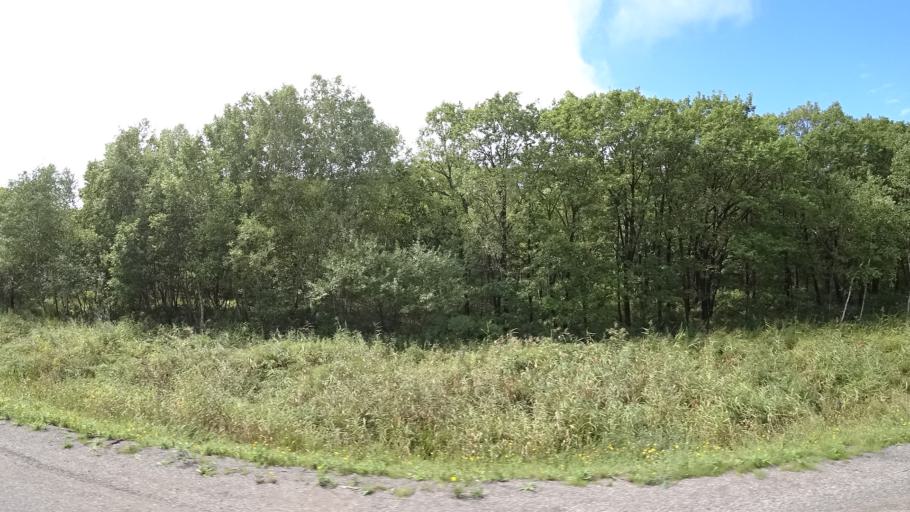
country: RU
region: Primorskiy
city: Lyalichi
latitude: 44.1190
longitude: 132.4195
